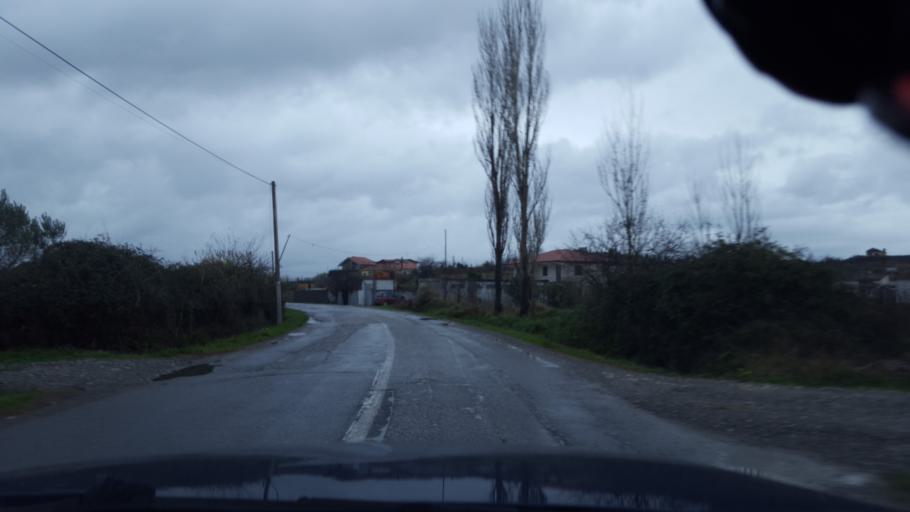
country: AL
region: Shkoder
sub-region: Rrethi i Shkodres
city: Berdica e Madhe
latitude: 42.0264
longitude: 19.4900
